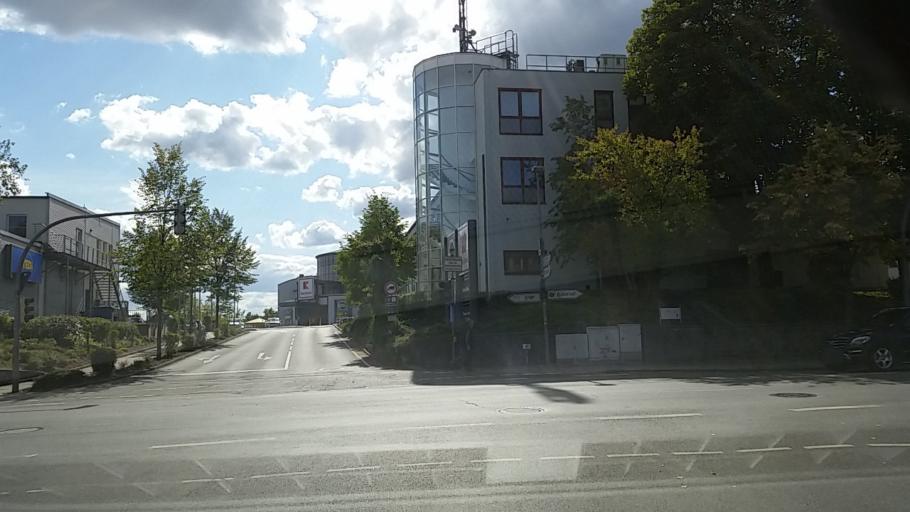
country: DE
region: Lower Saxony
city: Uelzen
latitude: 52.9677
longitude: 10.5539
